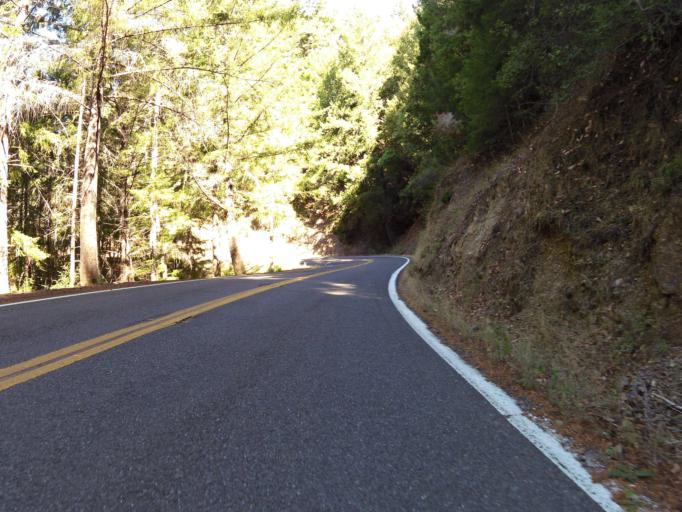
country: US
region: California
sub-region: Humboldt County
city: Redway
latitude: 39.8555
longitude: -123.7431
